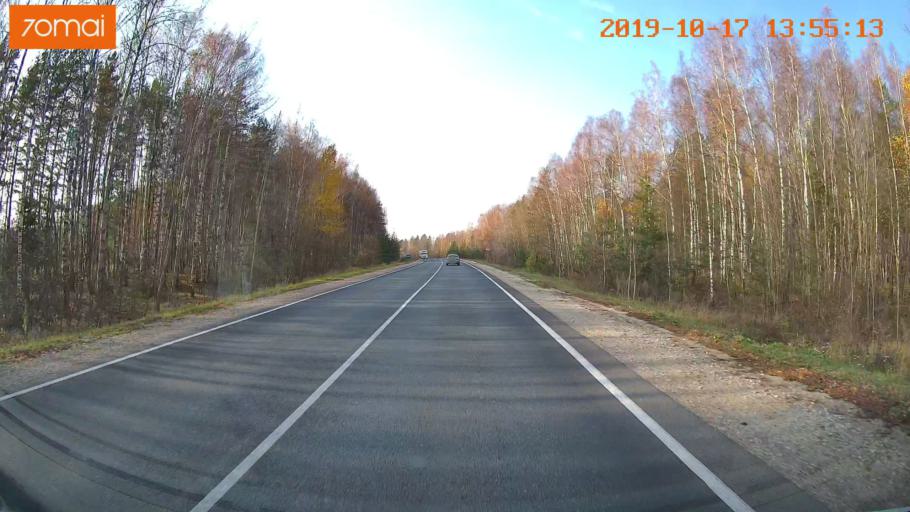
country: RU
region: Rjazan
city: Spas-Klepiki
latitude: 55.1510
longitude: 40.2950
